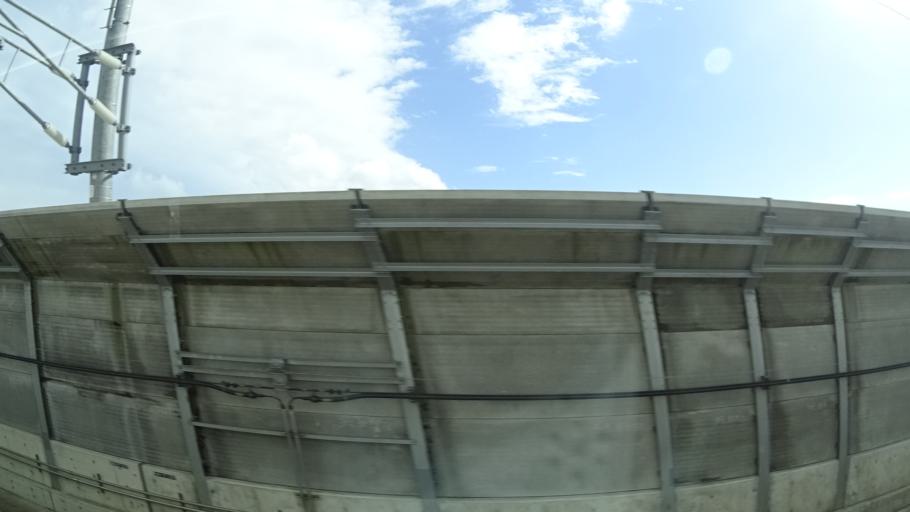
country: JP
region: Toyama
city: Takaoka
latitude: 36.7234
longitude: 137.0370
